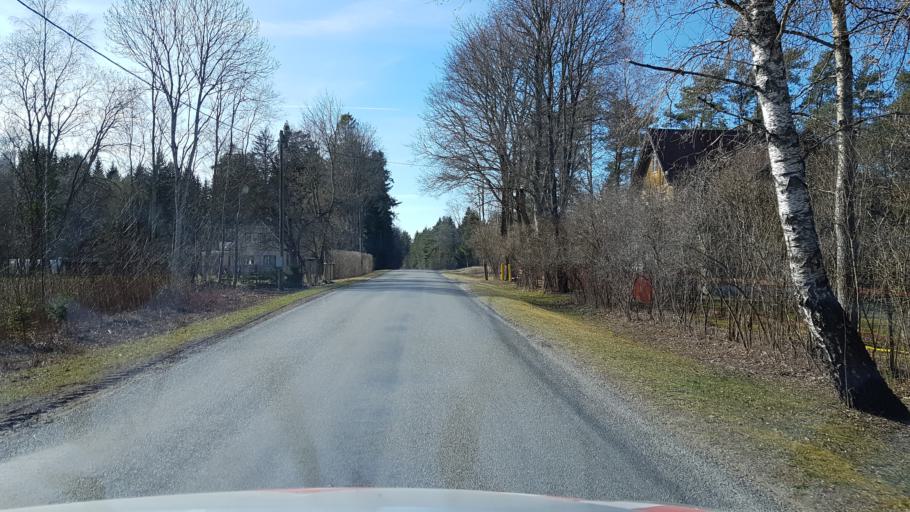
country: EE
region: Harju
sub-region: Nissi vald
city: Riisipere
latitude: 59.0978
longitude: 24.3340
